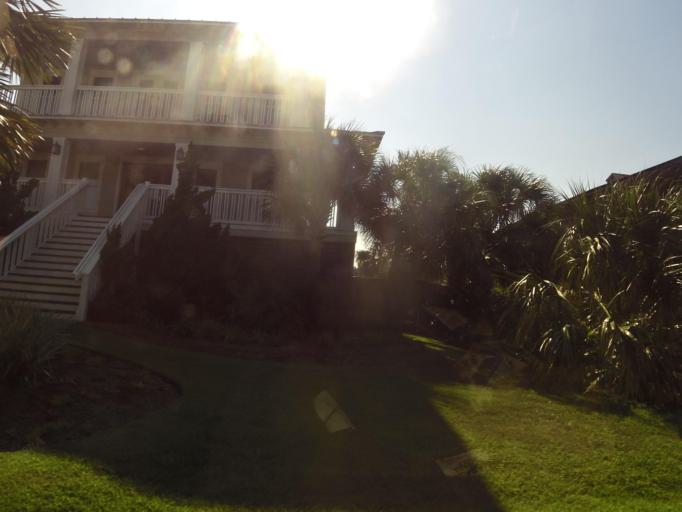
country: US
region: Florida
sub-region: Nassau County
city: Fernandina Beach
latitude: 30.6865
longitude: -81.4301
